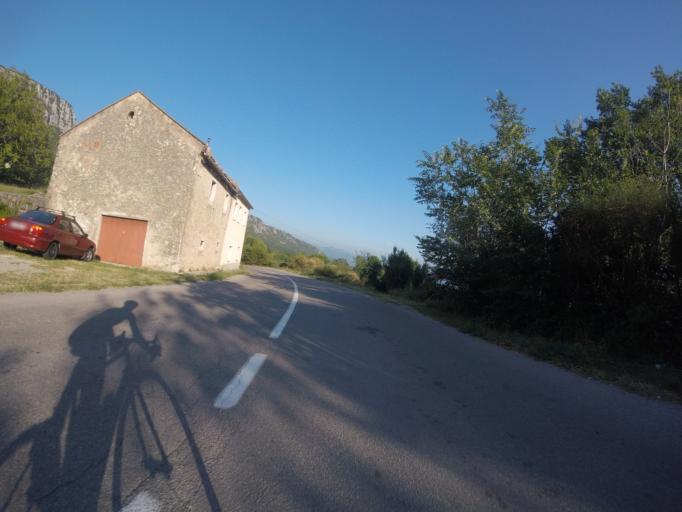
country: HR
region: Primorsko-Goranska
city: Bribir
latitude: 45.1734
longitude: 14.7447
